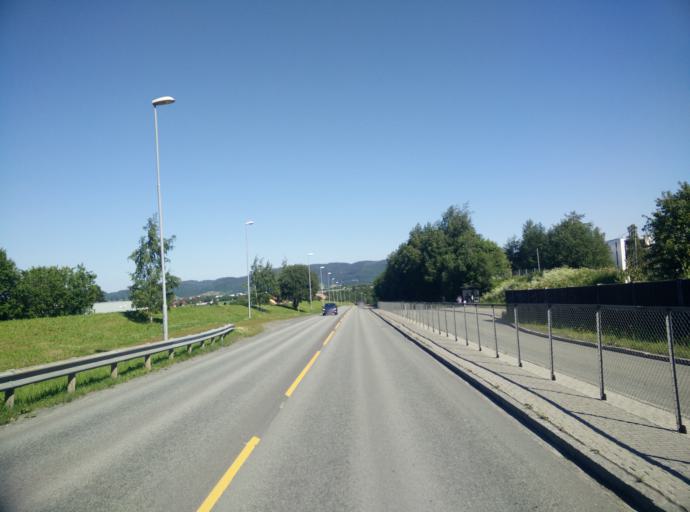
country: NO
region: Sor-Trondelag
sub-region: Trondheim
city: Trondheim
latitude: 63.3706
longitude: 10.3549
